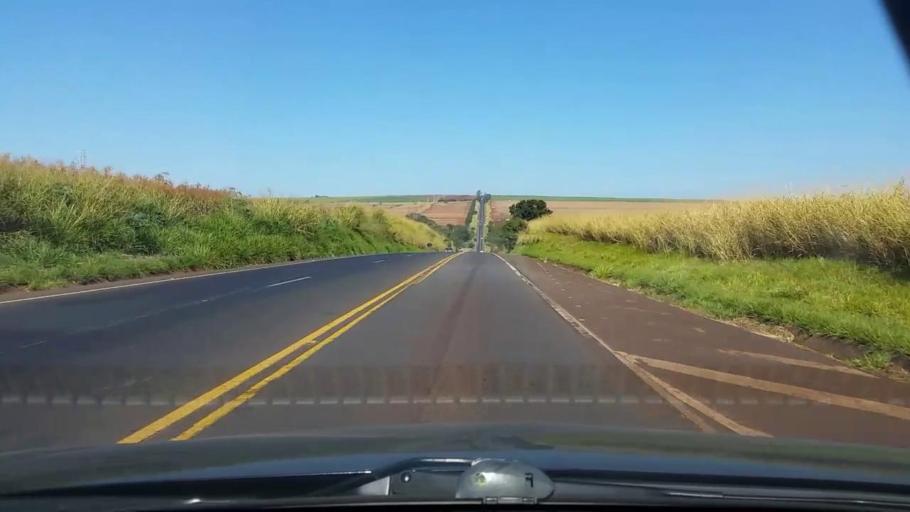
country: BR
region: Sao Paulo
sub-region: Jau
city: Jau
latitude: -22.3705
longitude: -48.5704
